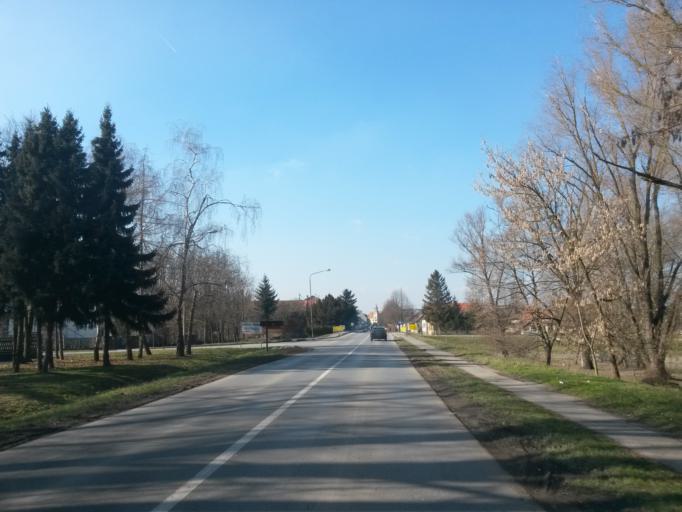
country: HR
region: Osjecko-Baranjska
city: Valpovo
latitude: 45.6550
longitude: 18.4258
